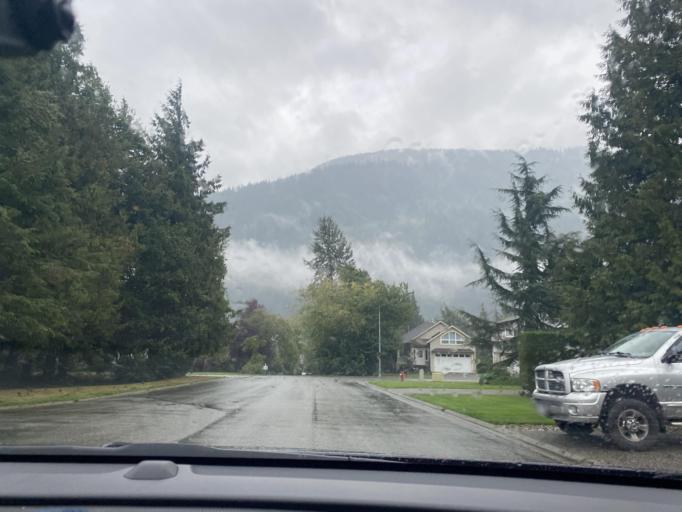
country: CA
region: British Columbia
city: Agassiz
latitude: 49.3010
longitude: -121.7813
